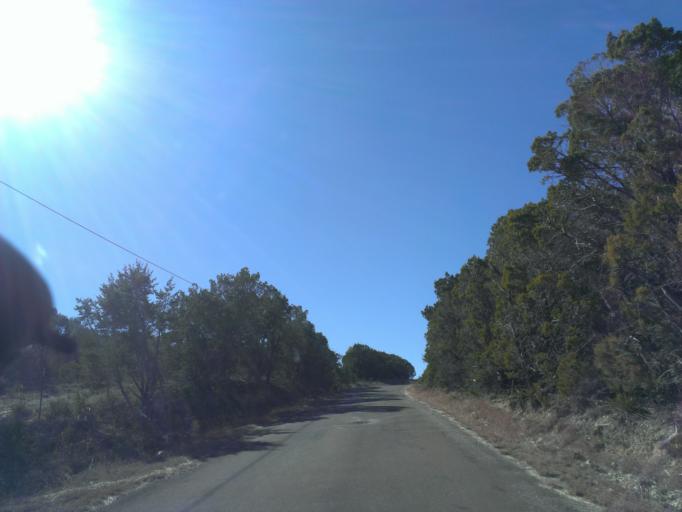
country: US
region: Texas
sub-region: Lampasas County
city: Lampasas
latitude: 30.9245
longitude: -98.1376
